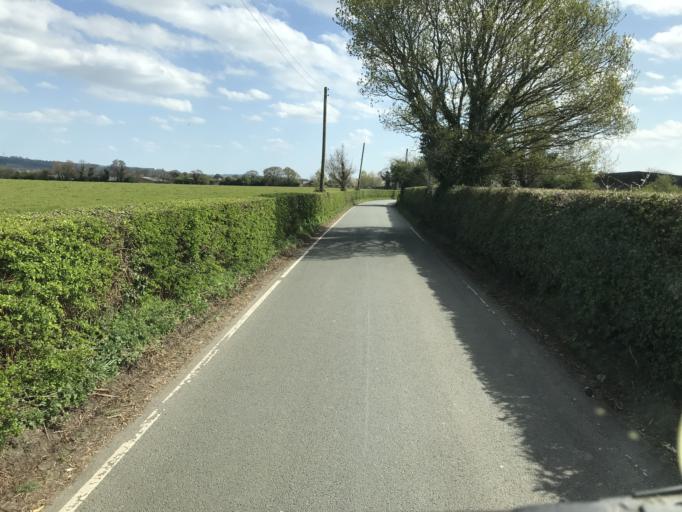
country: GB
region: England
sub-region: Cheshire West and Chester
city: Tarvin
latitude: 53.2108
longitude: -2.7698
